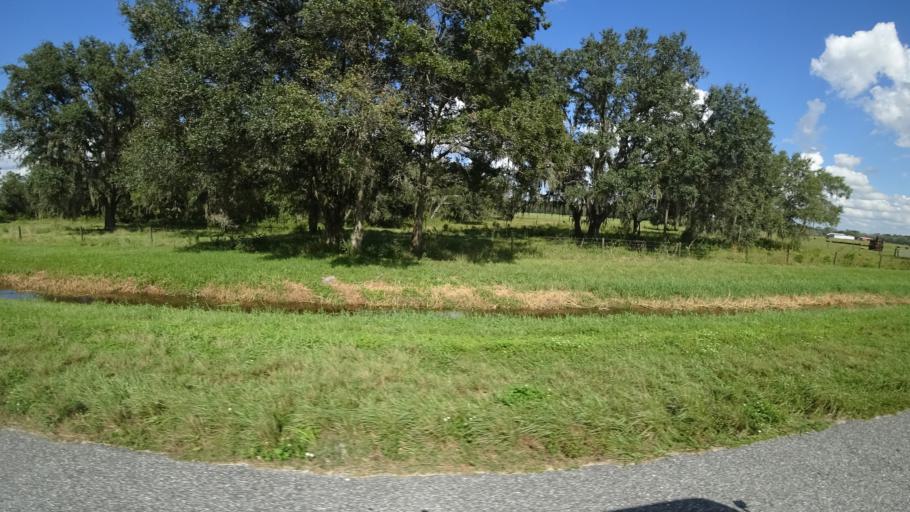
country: US
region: Florida
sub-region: Sarasota County
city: Warm Mineral Springs
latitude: 27.3366
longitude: -82.1383
